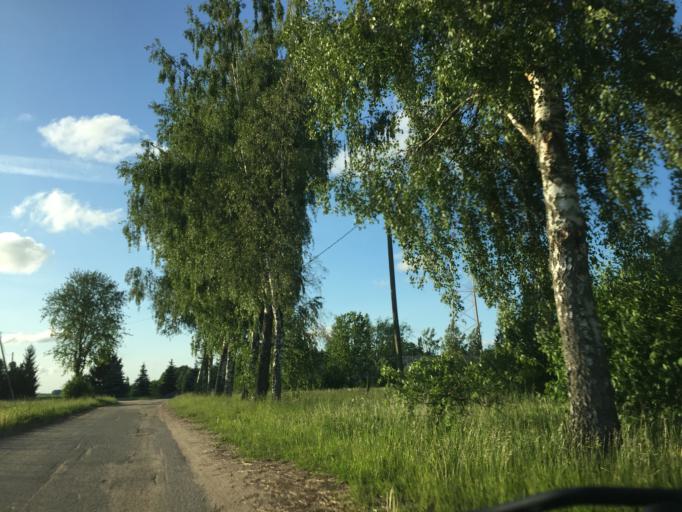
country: LV
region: Koceni
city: Koceni
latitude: 57.4719
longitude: 25.2636
